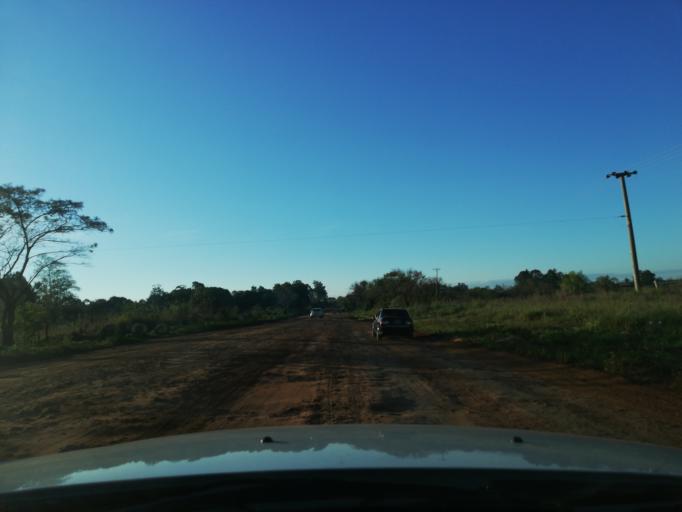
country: AR
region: Misiones
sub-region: Departamento de Capital
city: Posadas
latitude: -27.4703
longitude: -55.9708
